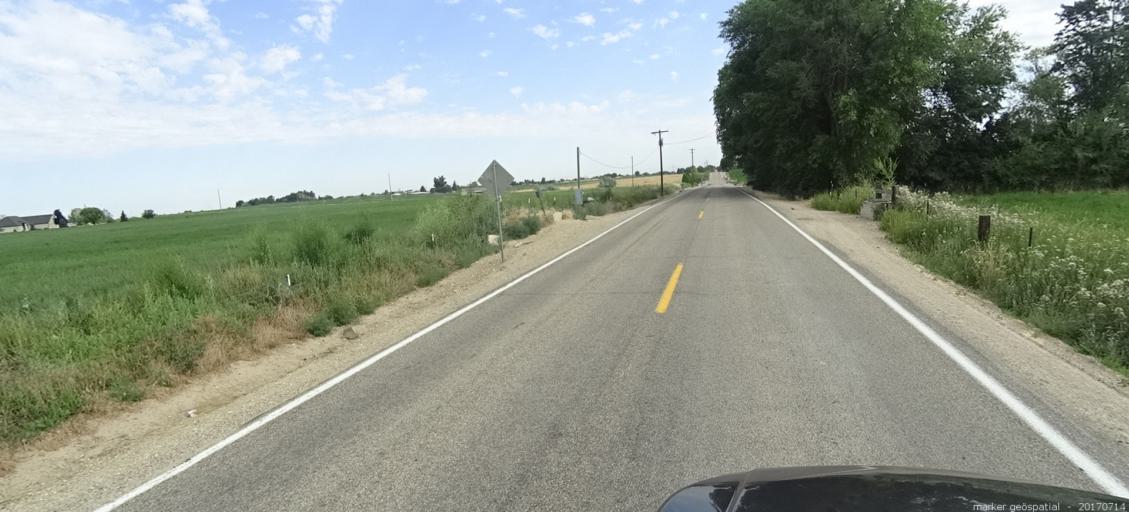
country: US
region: Idaho
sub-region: Ada County
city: Kuna
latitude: 43.4612
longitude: -116.3546
